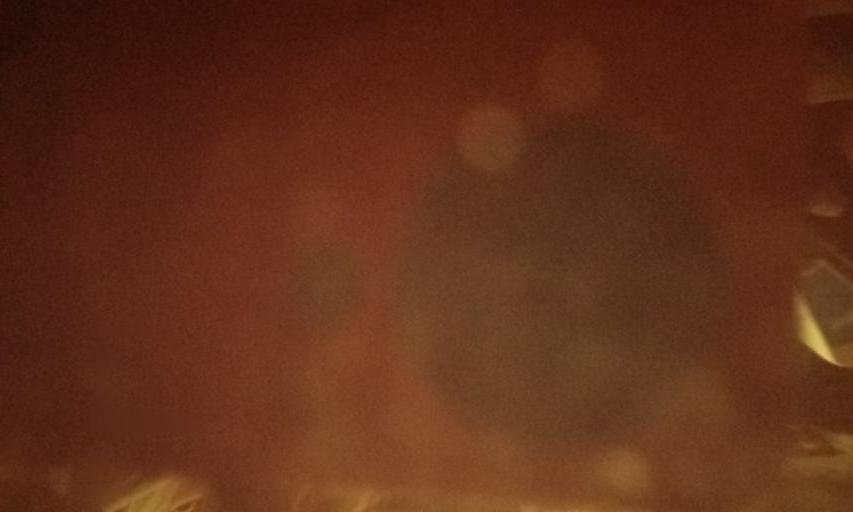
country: JP
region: Hyogo
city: Ashiya
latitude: 34.7332
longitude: 135.2680
